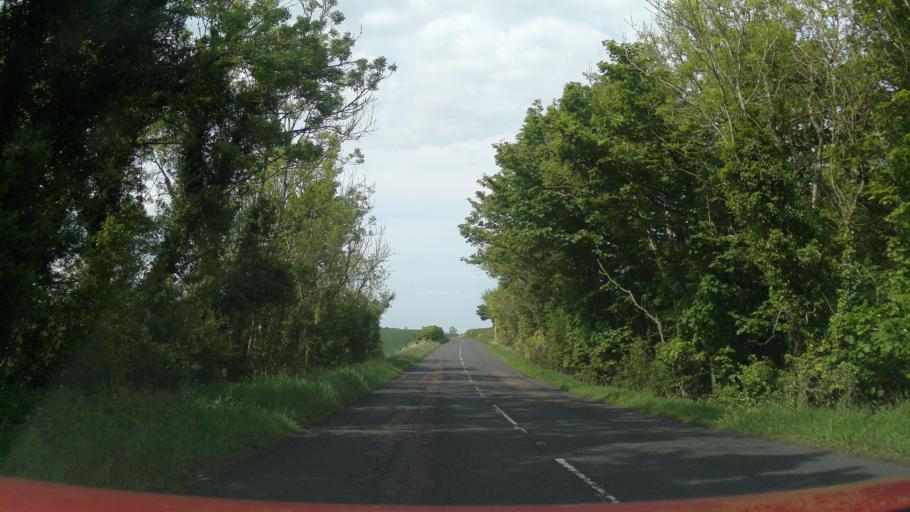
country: GB
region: England
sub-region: Northumberland
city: Ellingham
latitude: 55.4668
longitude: -1.7191
